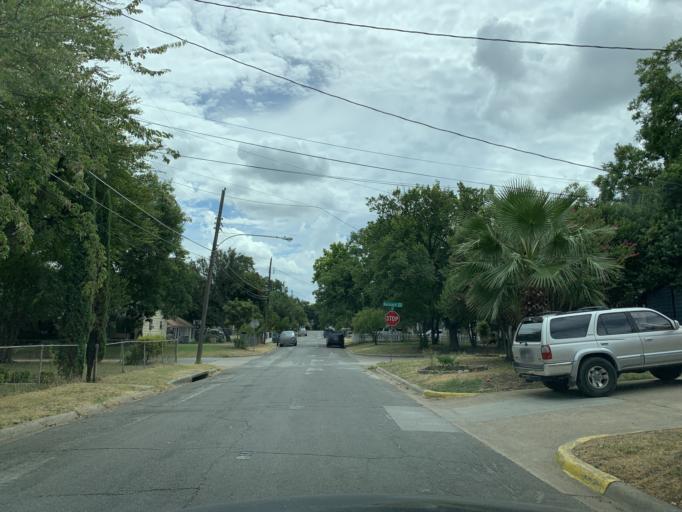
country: US
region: Texas
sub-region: Dallas County
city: Cockrell Hill
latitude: 32.7335
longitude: -96.8793
